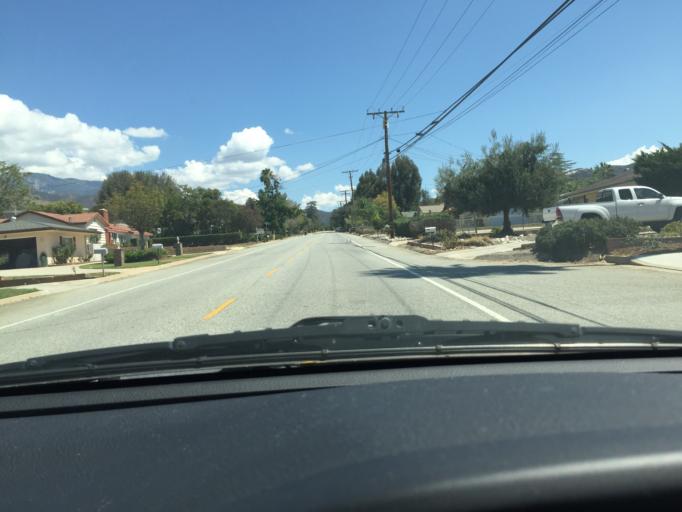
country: US
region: California
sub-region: San Bernardino County
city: Yucaipa
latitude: 34.0157
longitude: -117.0279
